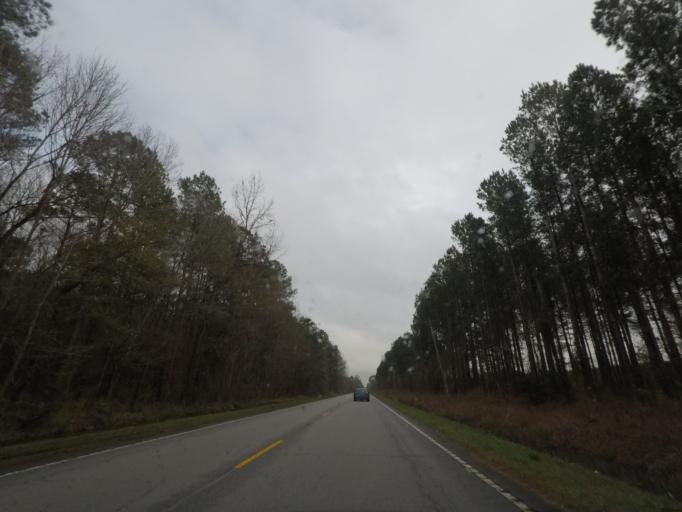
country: US
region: South Carolina
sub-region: Colleton County
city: Walterboro
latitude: 32.8155
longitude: -80.5385
